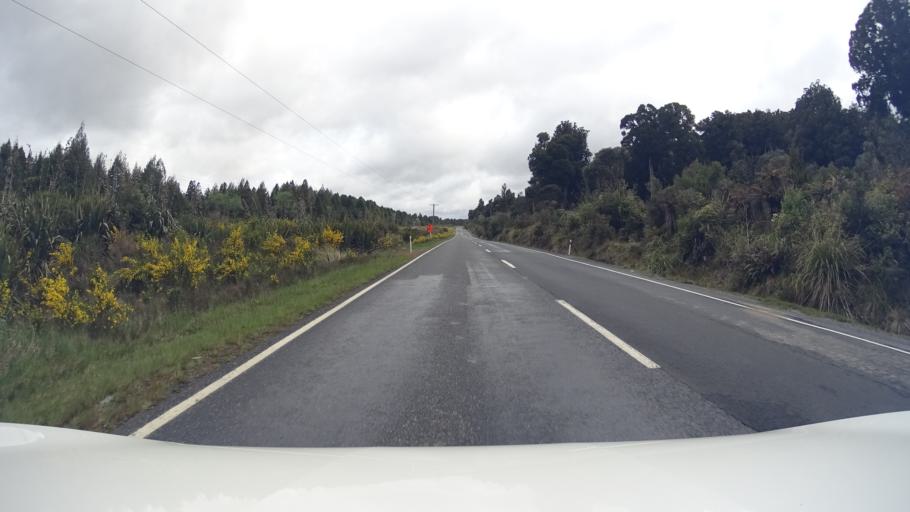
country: NZ
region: Manawatu-Wanganui
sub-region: Ruapehu District
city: Waiouru
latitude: -39.2536
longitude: 175.3880
